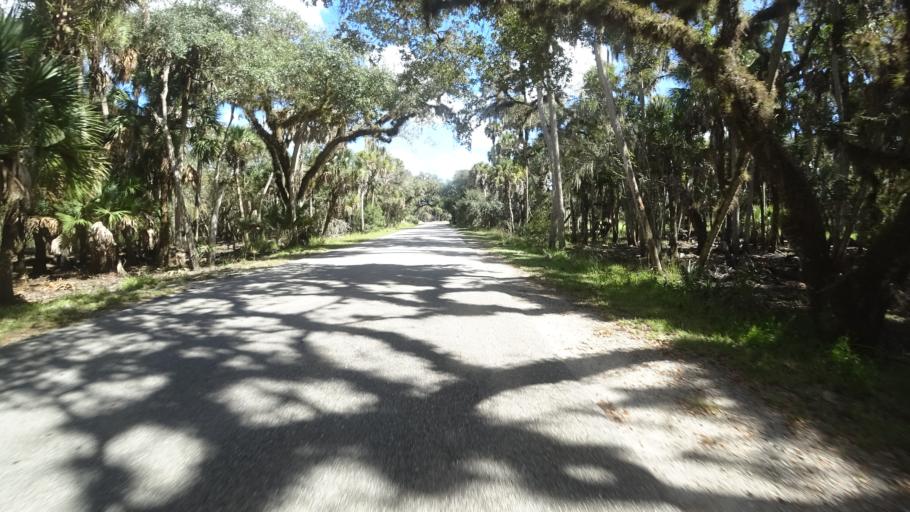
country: US
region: Florida
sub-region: Sarasota County
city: Lake Sarasota
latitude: 27.2475
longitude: -82.2980
